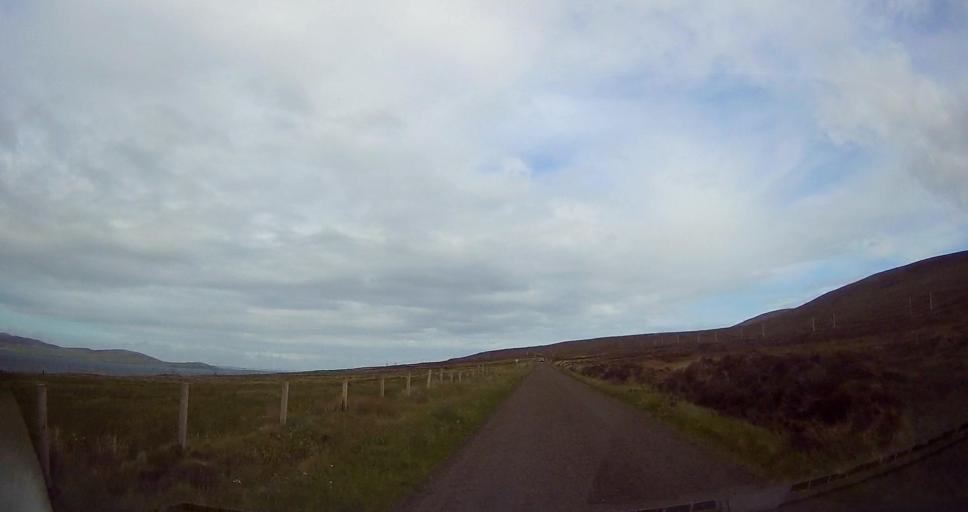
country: GB
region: Scotland
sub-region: Orkney Islands
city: Stromness
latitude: 58.9030
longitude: -3.3000
